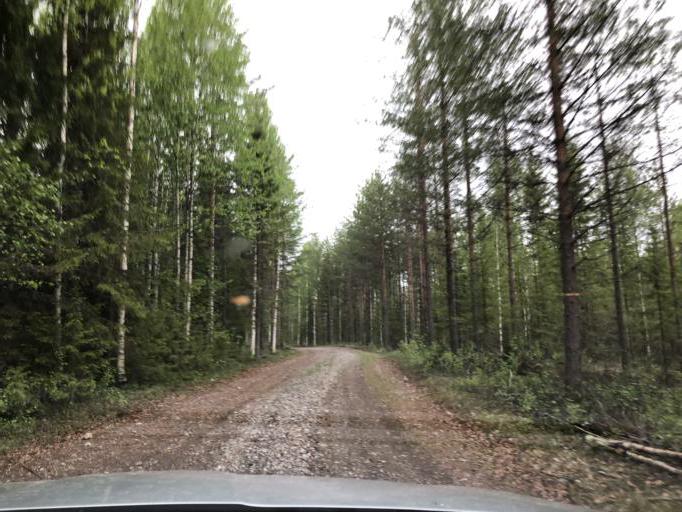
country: SE
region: Norrbotten
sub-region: Pitea Kommun
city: Roknas
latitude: 65.4005
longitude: 21.2625
